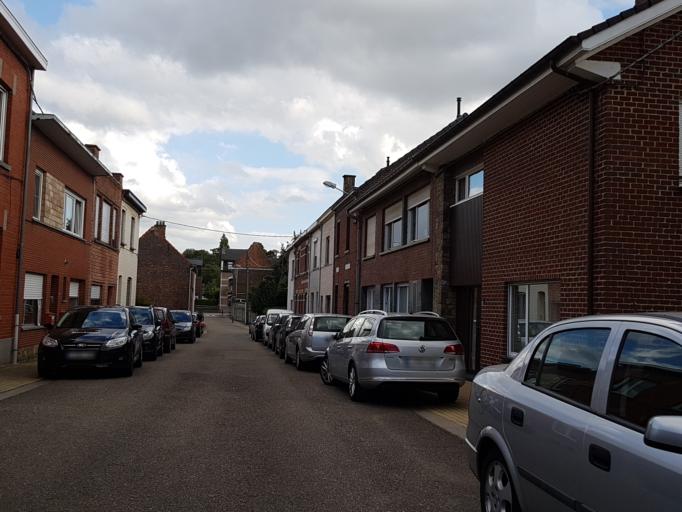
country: BE
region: Flanders
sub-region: Provincie Vlaams-Brabant
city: Kortenberg
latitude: 50.8945
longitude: 4.5430
